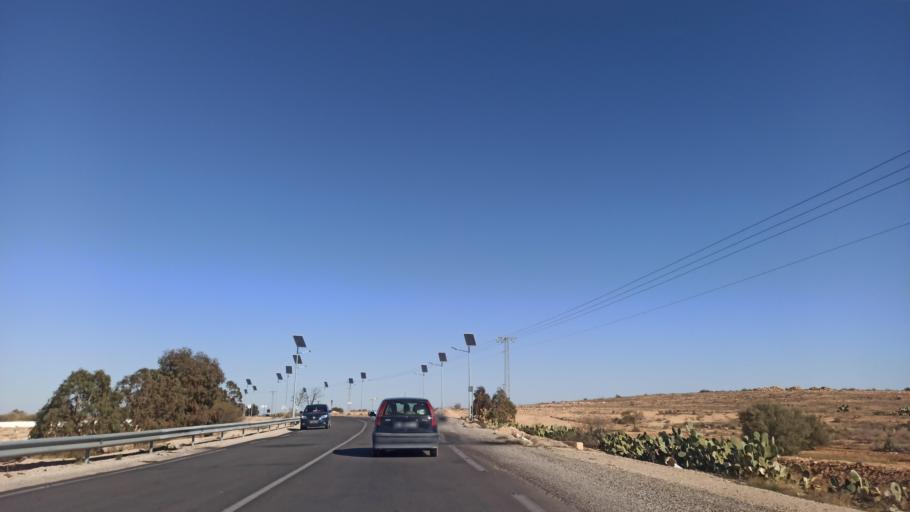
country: TN
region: Sidi Bu Zayd
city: Bi'r al Hufayy
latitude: 34.7246
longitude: 9.0629
